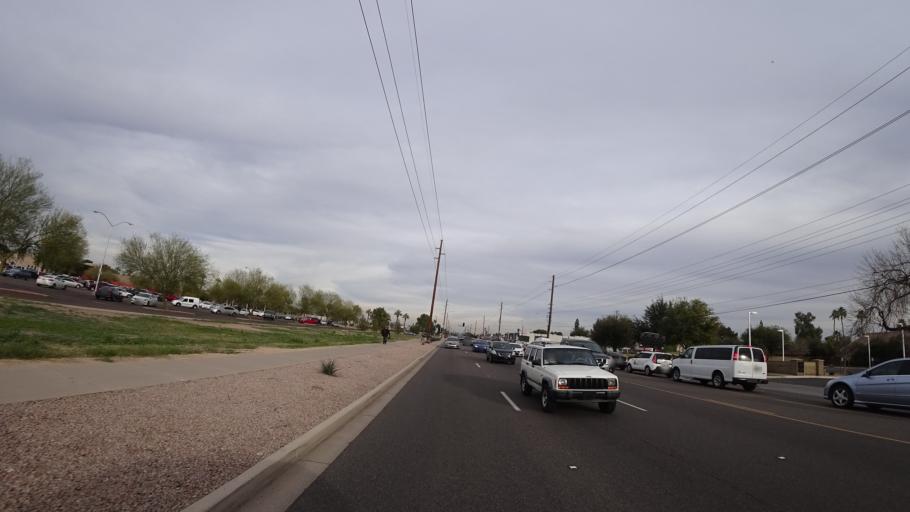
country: US
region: Arizona
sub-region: Maricopa County
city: Glendale
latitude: 33.5675
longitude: -112.1921
